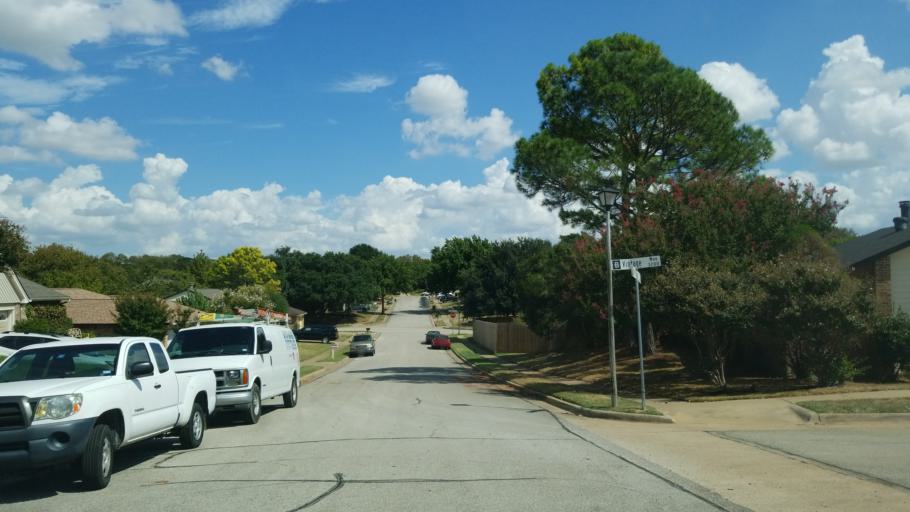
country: US
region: Texas
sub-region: Tarrant County
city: Bedford
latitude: 32.8589
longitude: -97.1113
